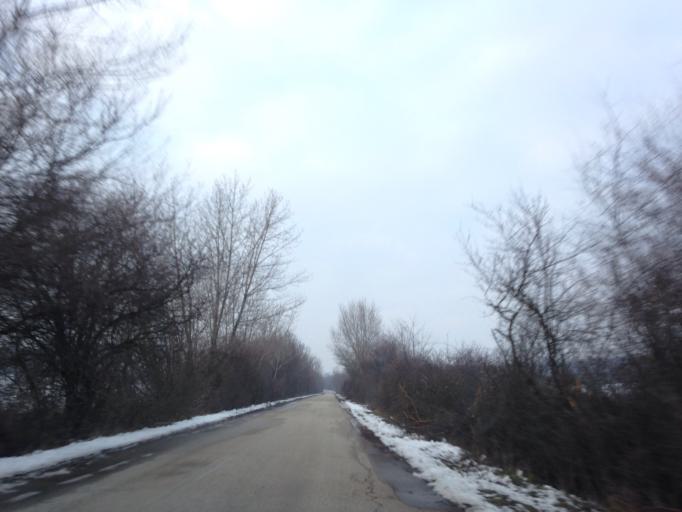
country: SK
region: Nitriansky
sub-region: Okres Nitra
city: Vrable
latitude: 48.0891
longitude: 18.3692
